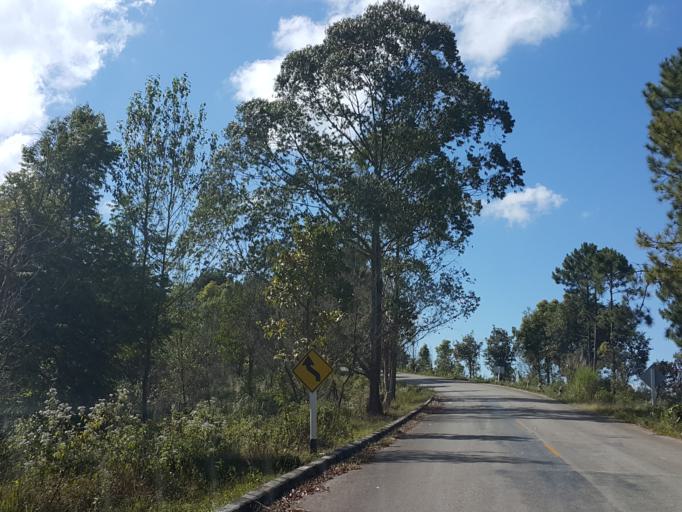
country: TH
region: Chiang Mai
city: Wiang Haeng
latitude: 19.5192
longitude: 98.7601
